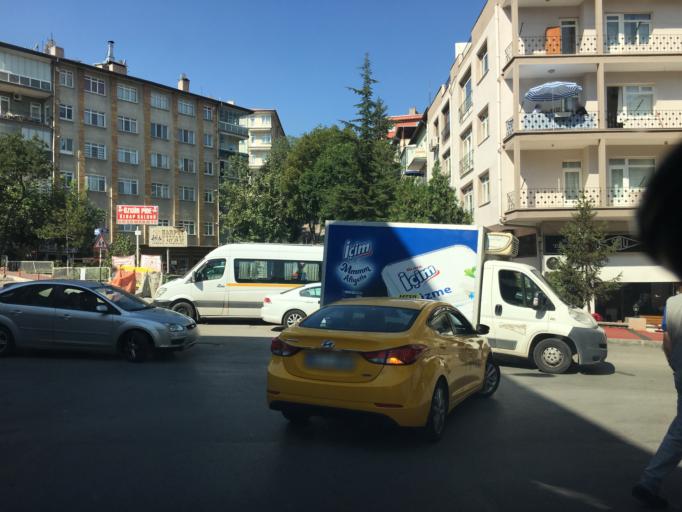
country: TR
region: Ankara
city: Ankara
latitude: 39.8977
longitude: 32.8507
